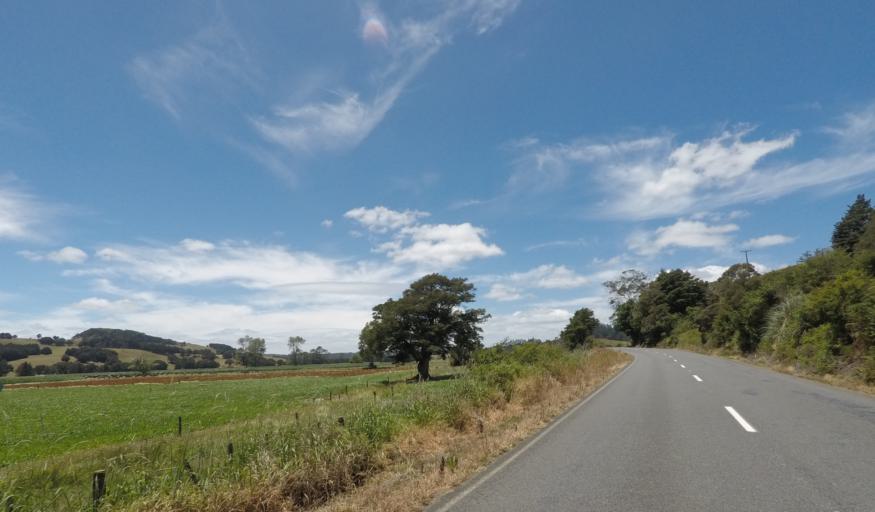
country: NZ
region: Northland
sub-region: Whangarei
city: Whangarei
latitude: -35.5350
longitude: 174.3154
